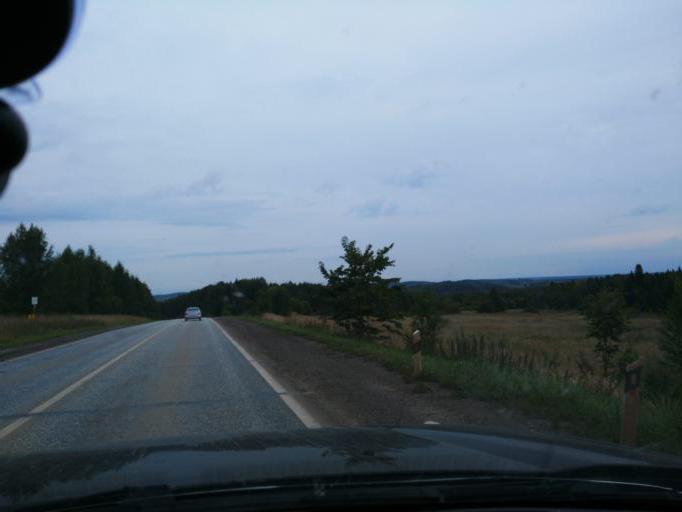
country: RU
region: Perm
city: Chernushka
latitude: 56.5897
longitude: 56.1525
